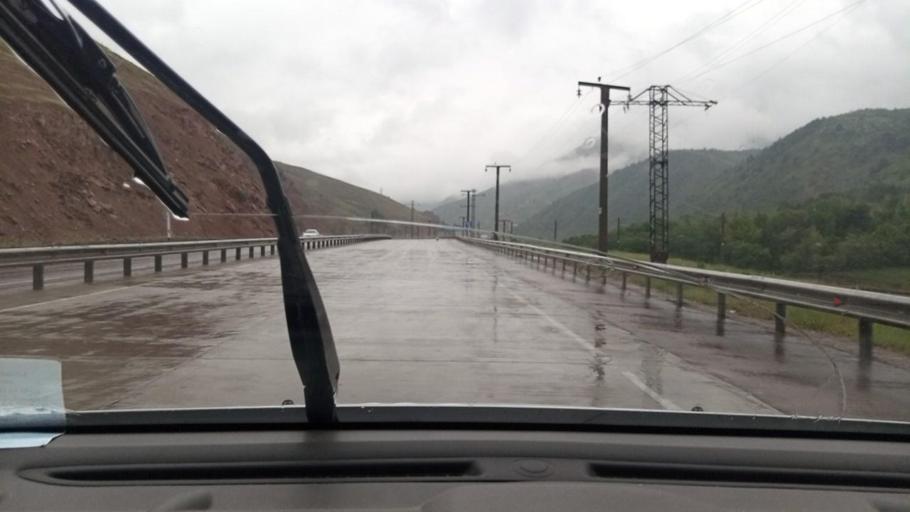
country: UZ
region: Toshkent
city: Angren
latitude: 41.1475
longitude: 70.4150
